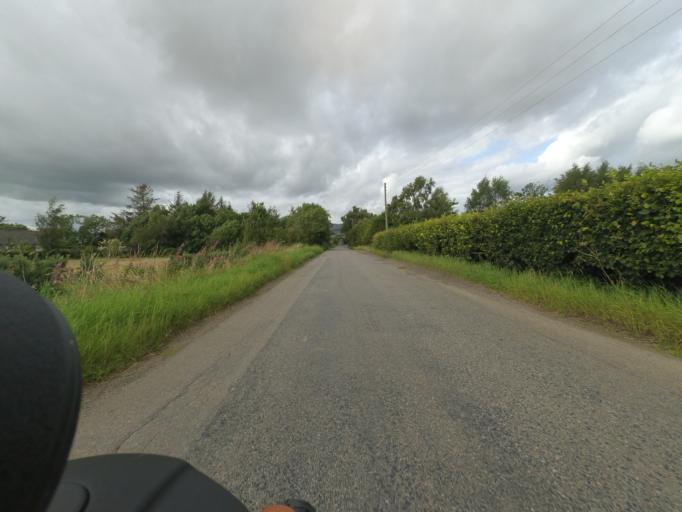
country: GB
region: Scotland
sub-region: Aberdeenshire
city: Laurencekirk
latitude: 56.8402
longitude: -2.5663
